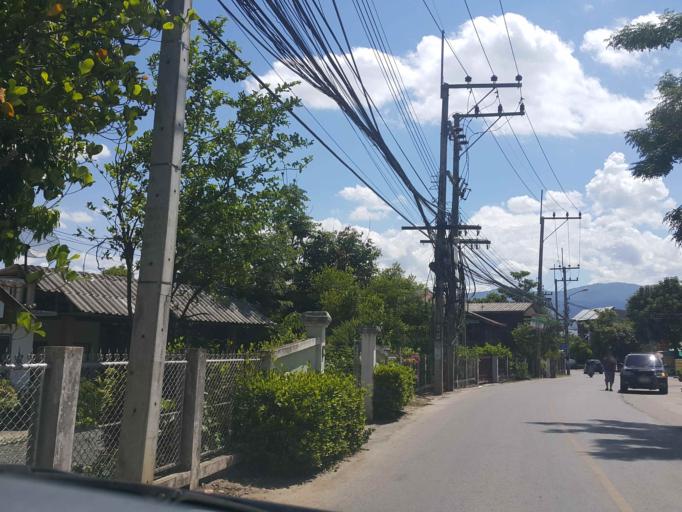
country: TH
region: Chiang Mai
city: San Sai
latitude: 18.8487
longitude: 99.0229
